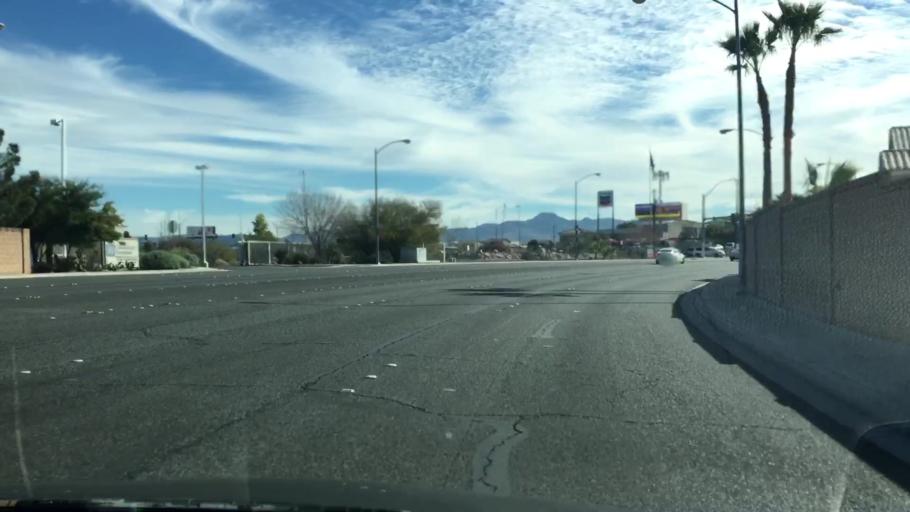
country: US
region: Nevada
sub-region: Clark County
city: Paradise
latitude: 36.0440
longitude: -115.1366
